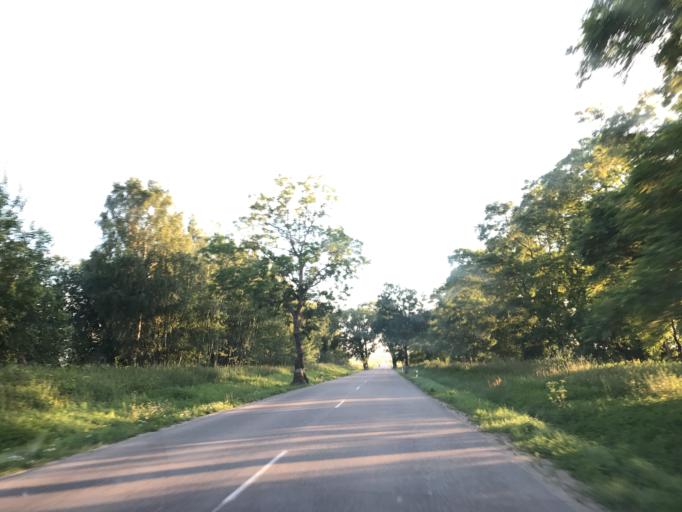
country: RU
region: Kaliningrad
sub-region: Zelenogradskiy Rayon
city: Zelenogradsk
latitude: 54.9358
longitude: 20.4421
